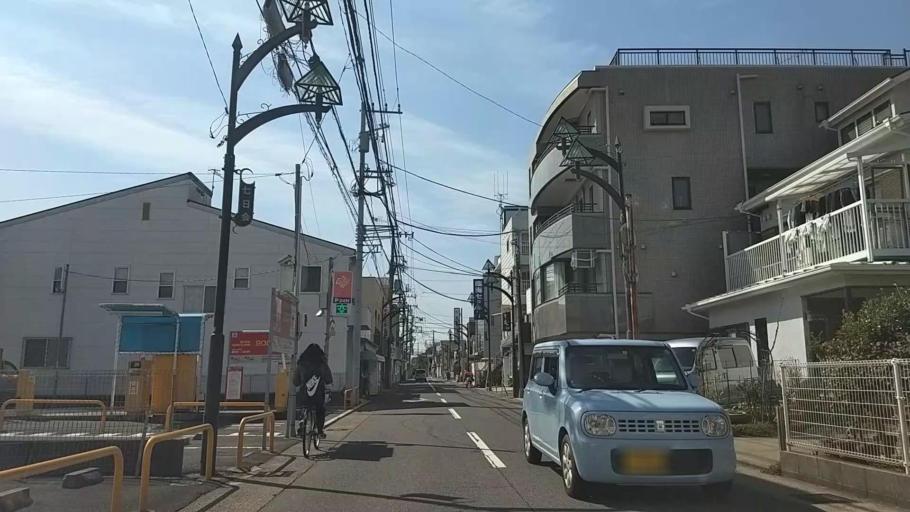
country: JP
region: Kanagawa
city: Fujisawa
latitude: 35.4129
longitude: 139.4640
